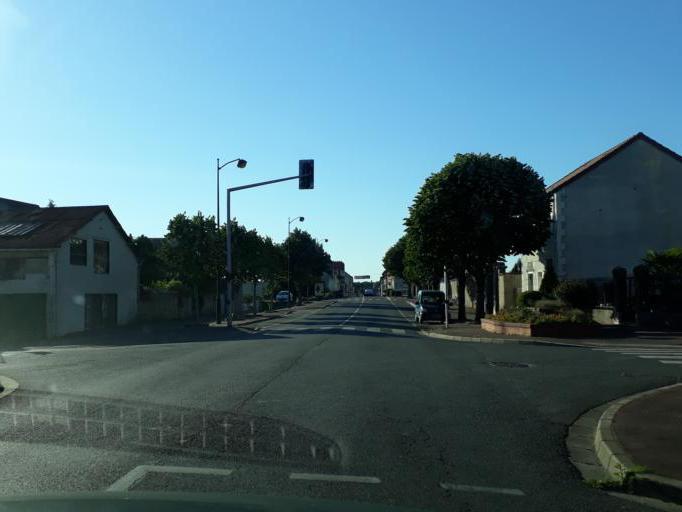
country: FR
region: Centre
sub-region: Departement du Loiret
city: Briare
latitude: 47.6350
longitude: 2.7432
